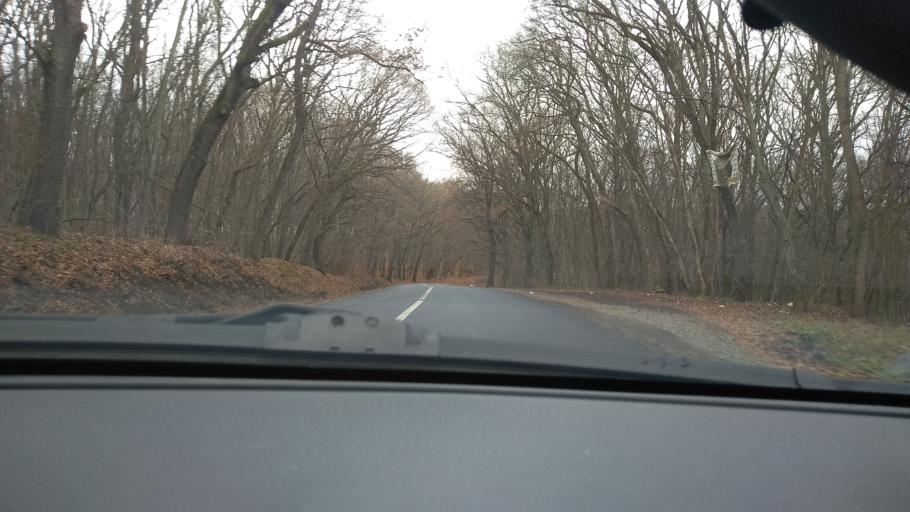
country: RO
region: Mures
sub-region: Comuna Pasareni
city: Pasareni
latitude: 46.5324
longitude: 24.6978
